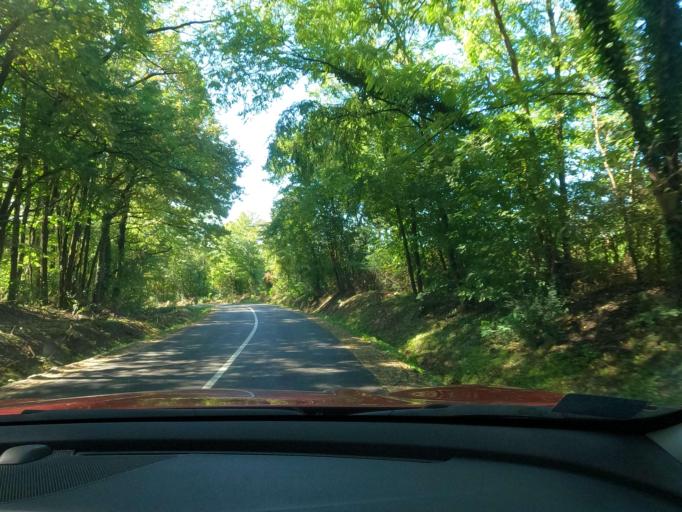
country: HR
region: Sisacko-Moslavacka
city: Petrinja
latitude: 45.4658
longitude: 16.2702
